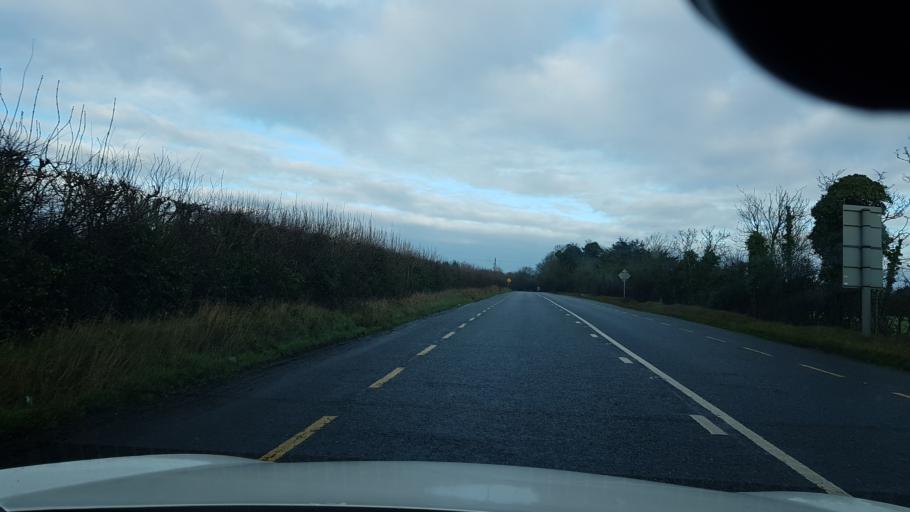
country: IE
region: Leinster
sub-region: An Mhi
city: Dunshaughlin
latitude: 53.5696
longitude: -6.5806
